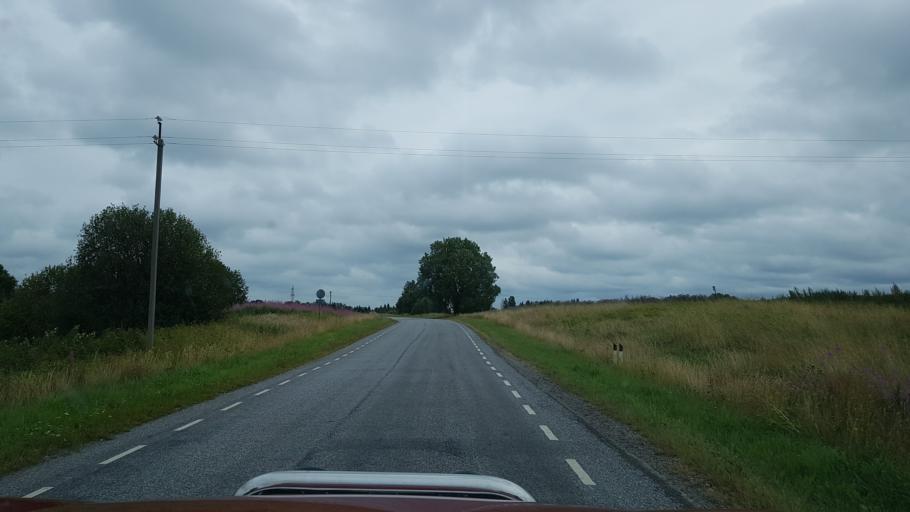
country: EE
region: Ida-Virumaa
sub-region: Puessi linn
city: Pussi
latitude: 59.3773
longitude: 27.0381
